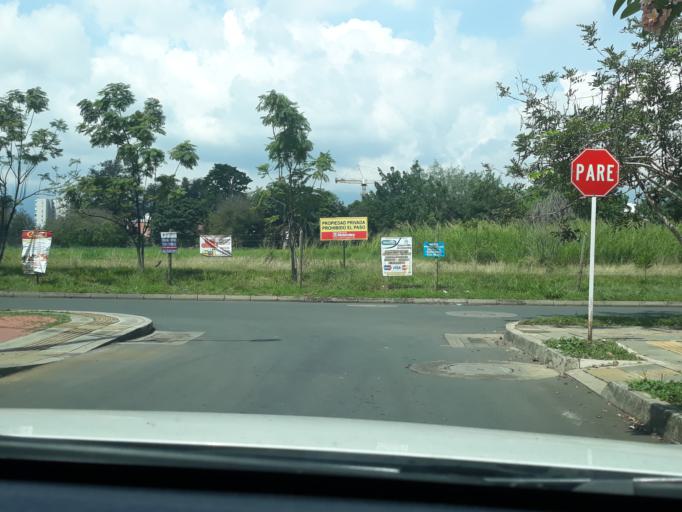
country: CO
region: Valle del Cauca
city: Cali
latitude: 3.3697
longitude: -76.5116
